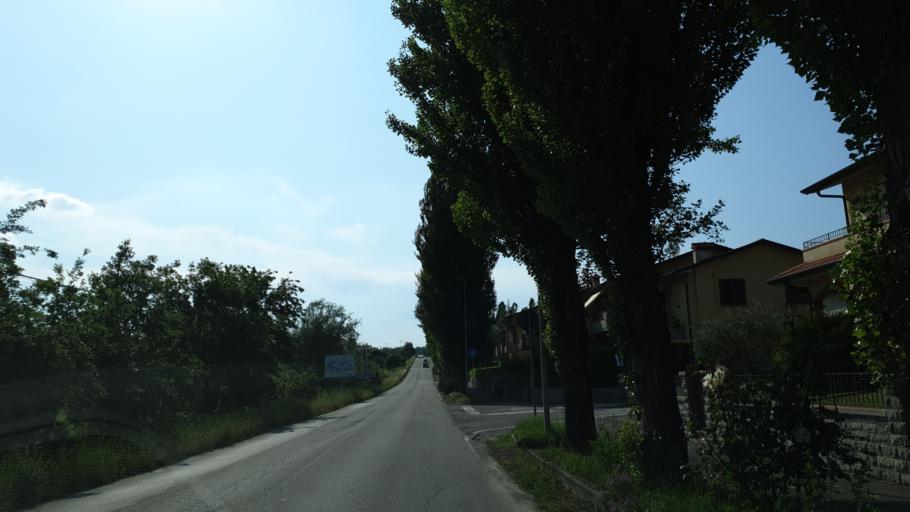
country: IT
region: Tuscany
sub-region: Province of Arezzo
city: Soci
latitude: 43.7373
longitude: 11.8082
